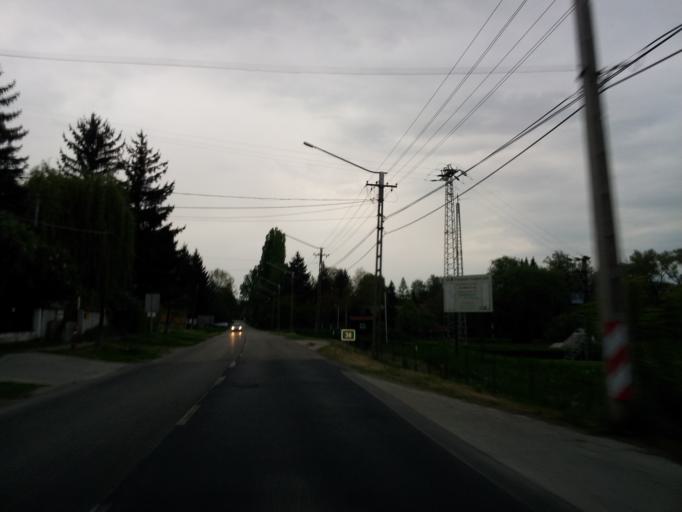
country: HU
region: Pest
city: Dunabogdany
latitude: 47.8008
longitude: 19.0159
